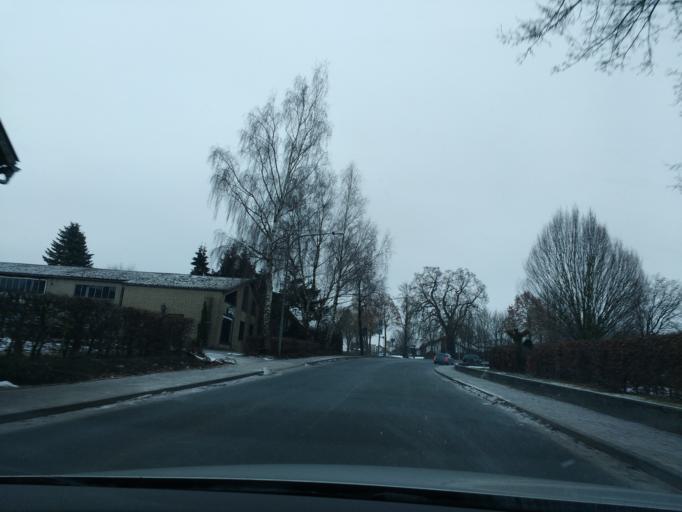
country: DE
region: North Rhine-Westphalia
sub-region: Regierungsbezirk Detmold
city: Wunnenberg
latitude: 51.5166
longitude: 8.6973
